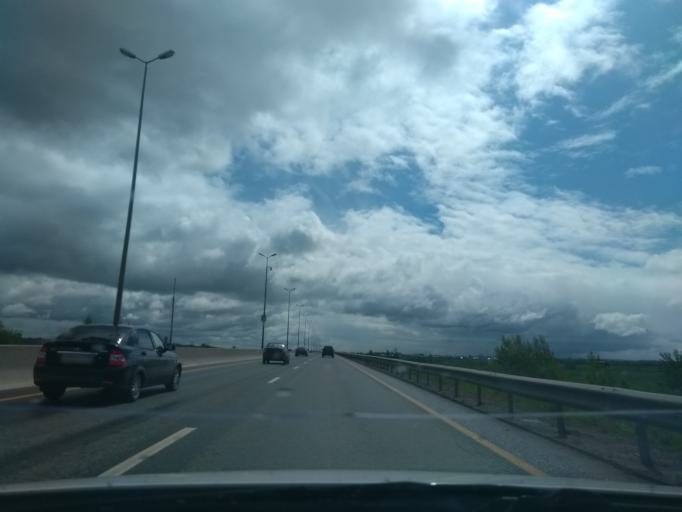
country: RU
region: Perm
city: Kondratovo
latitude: 57.9798
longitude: 56.0780
